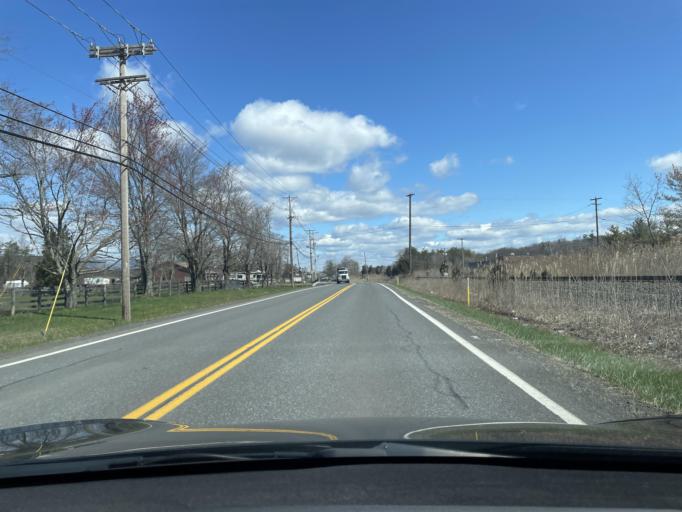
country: US
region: New York
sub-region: Ulster County
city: Saugerties South
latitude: 42.0514
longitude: -73.9793
